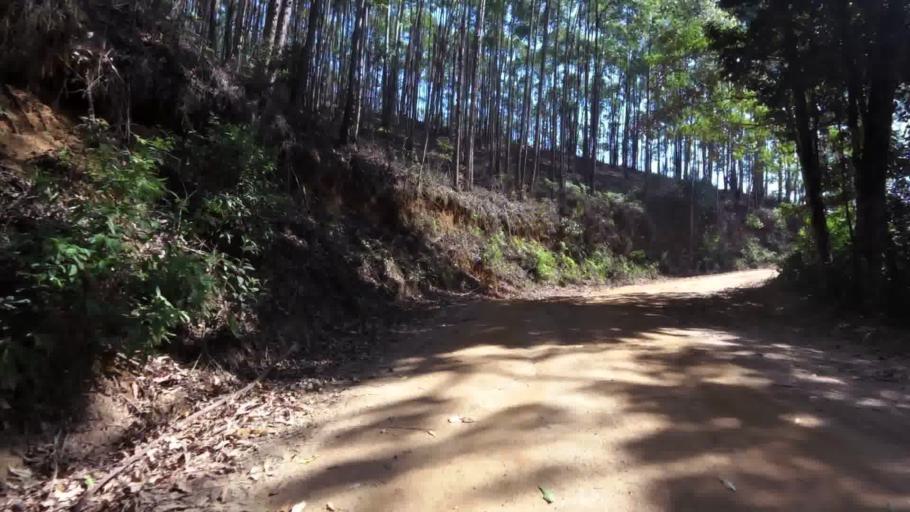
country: BR
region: Espirito Santo
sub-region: Alfredo Chaves
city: Alfredo Chaves
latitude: -20.5187
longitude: -40.8738
